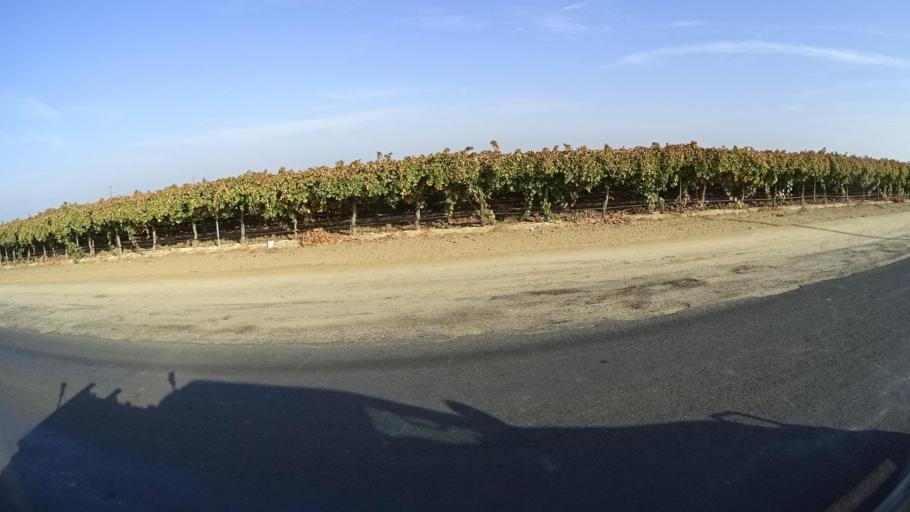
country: US
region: California
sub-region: Kern County
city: McFarland
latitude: 35.6746
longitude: -119.2032
